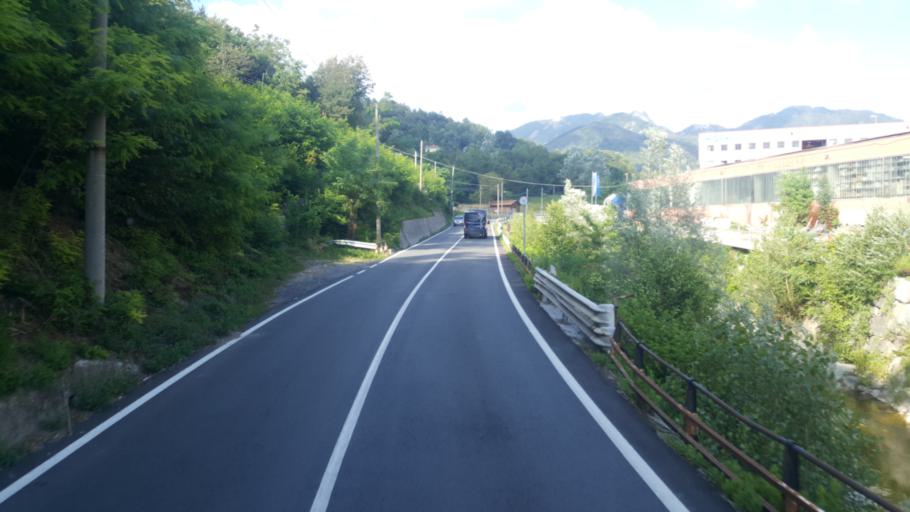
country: IT
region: Liguria
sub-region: Provincia di Genova
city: Savignone
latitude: 44.5807
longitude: 8.9729
